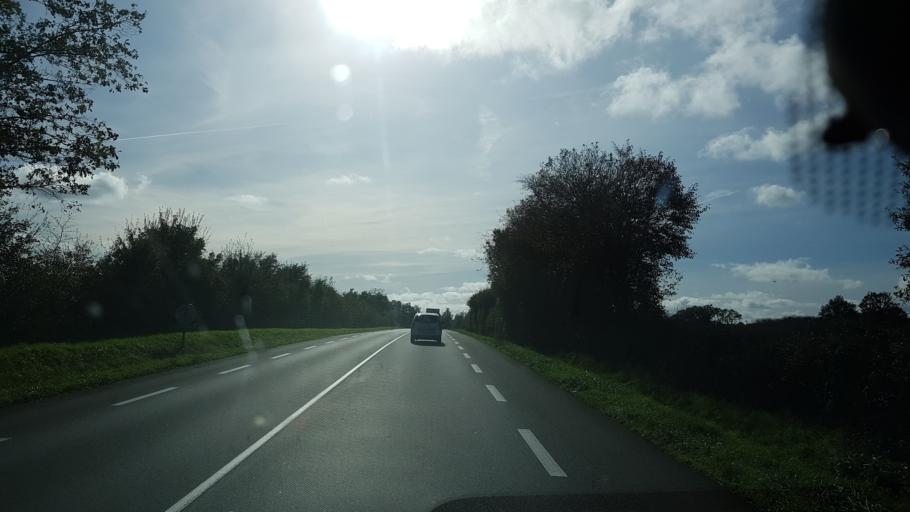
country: FR
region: Poitou-Charentes
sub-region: Departement de la Charente
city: Saint-Claud
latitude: 45.9117
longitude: 0.4929
